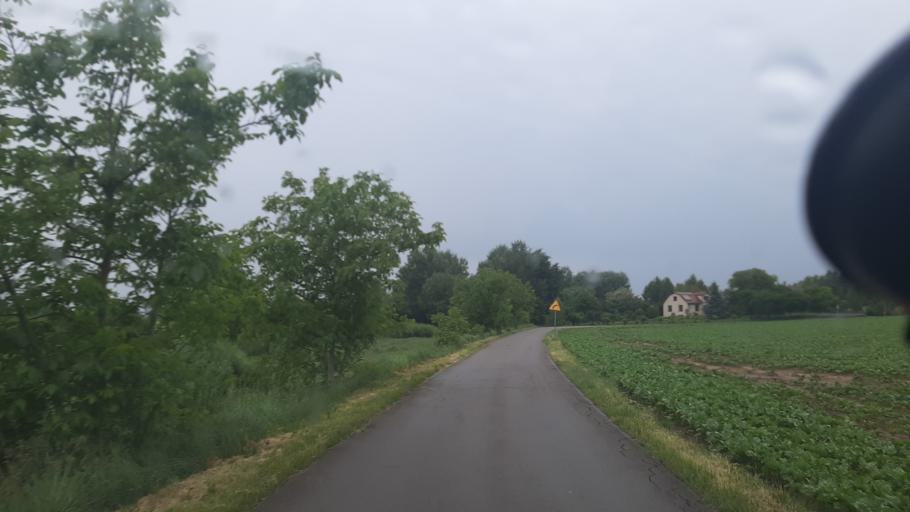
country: PL
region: Lublin Voivodeship
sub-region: Powiat lubelski
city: Garbow
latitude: 51.3531
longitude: 22.3430
